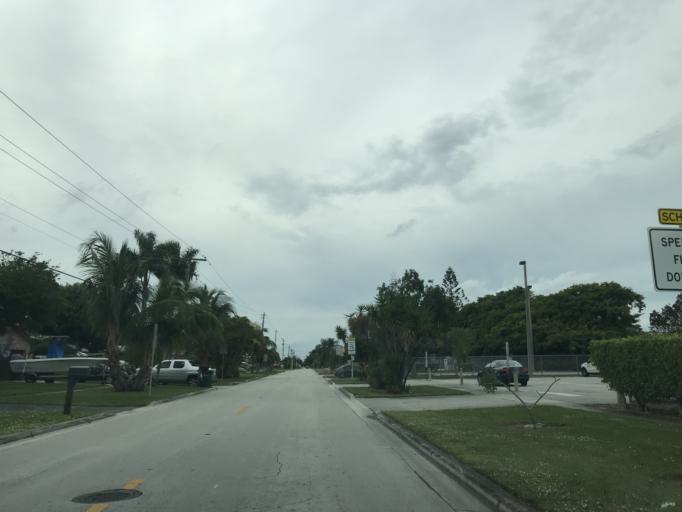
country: US
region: Florida
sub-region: Broward County
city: Margate
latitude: 26.2501
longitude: -80.2082
